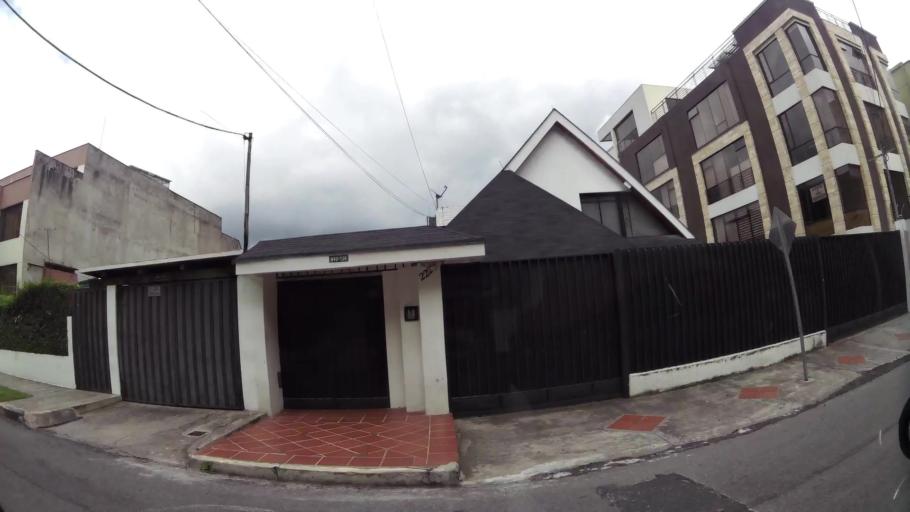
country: EC
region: Pichincha
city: Quito
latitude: -0.1672
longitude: -78.4950
